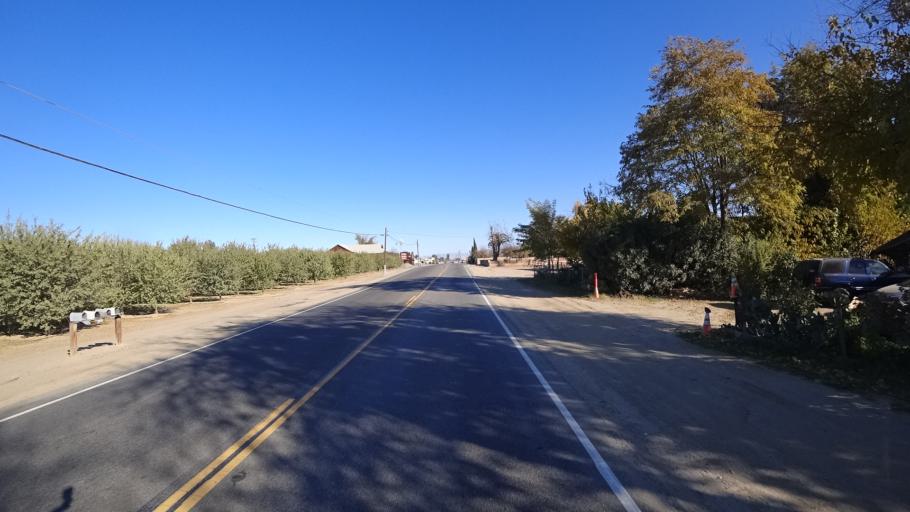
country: US
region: California
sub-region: Kern County
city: Greenfield
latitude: 35.2672
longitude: -119.1123
